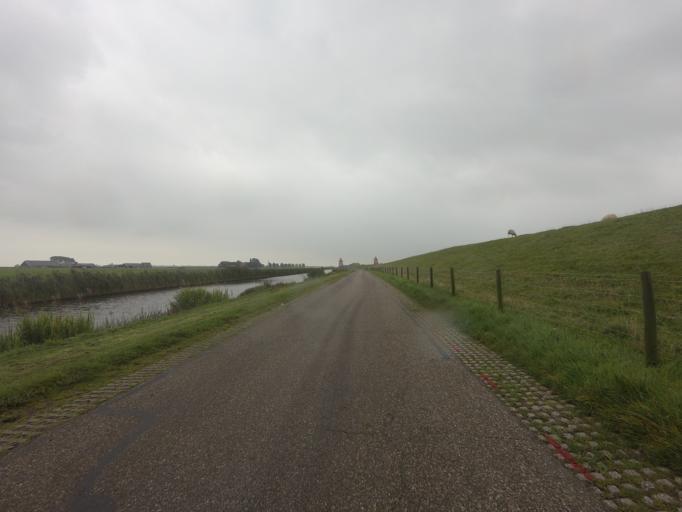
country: NL
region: Friesland
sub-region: Sudwest Fryslan
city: Koudum
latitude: 52.9304
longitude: 5.4060
